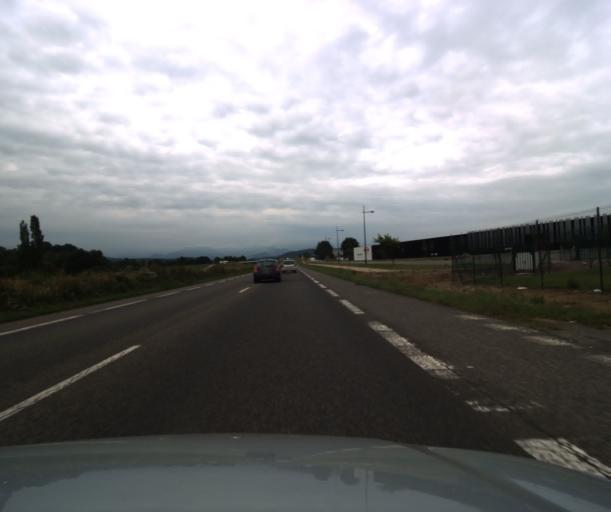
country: FR
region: Midi-Pyrenees
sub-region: Departement des Hautes-Pyrenees
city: Juillan
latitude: 43.1759
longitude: 0.0039
